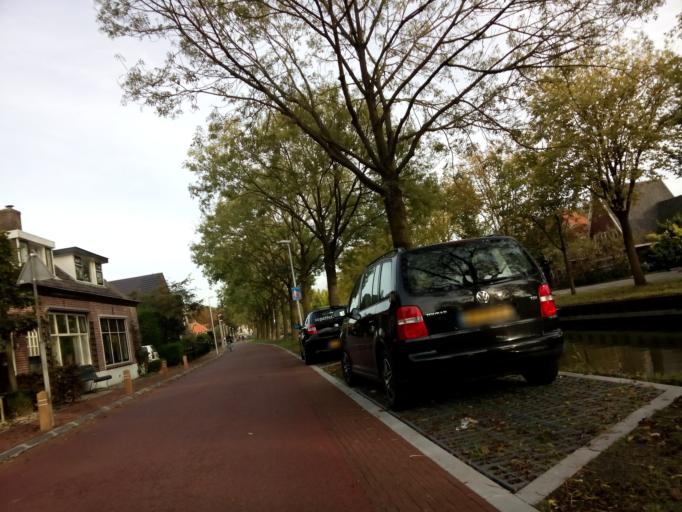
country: NL
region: Utrecht
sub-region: Gemeente Nieuwegein
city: Nieuwegein
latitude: 52.0825
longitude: 5.0636
